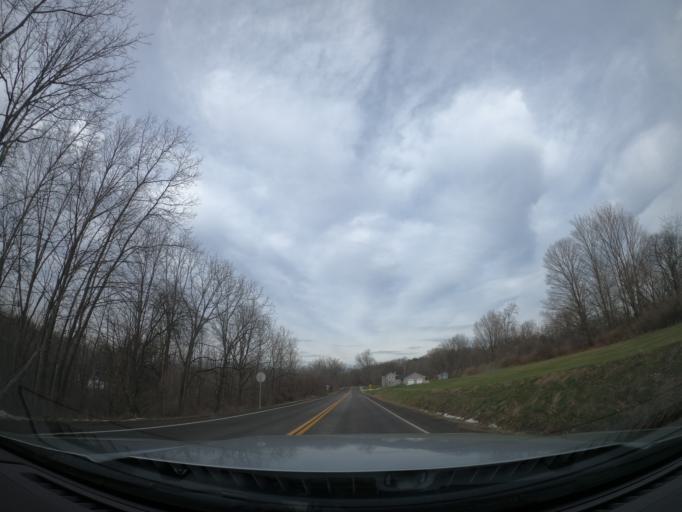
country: US
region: New York
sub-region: Yates County
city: Dundee
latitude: 42.5082
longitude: -76.9628
